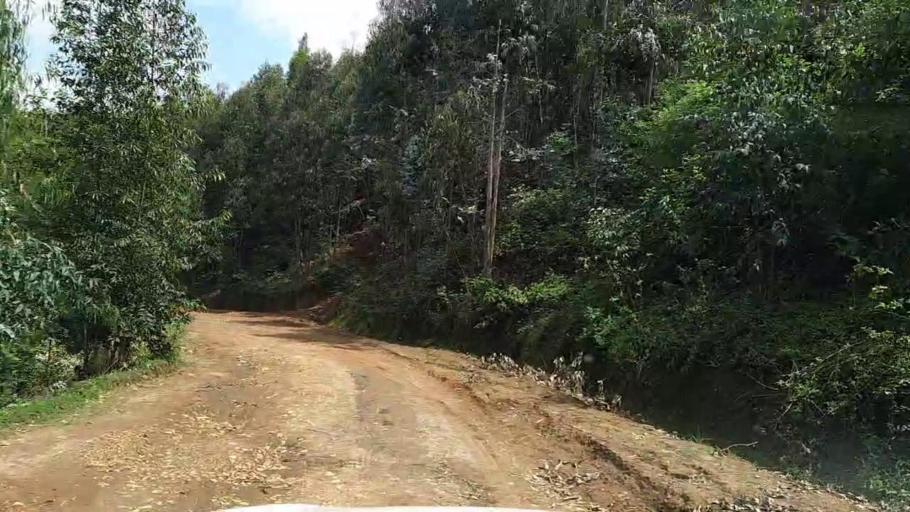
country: RW
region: Southern Province
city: Gikongoro
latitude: -2.3400
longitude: 29.5151
